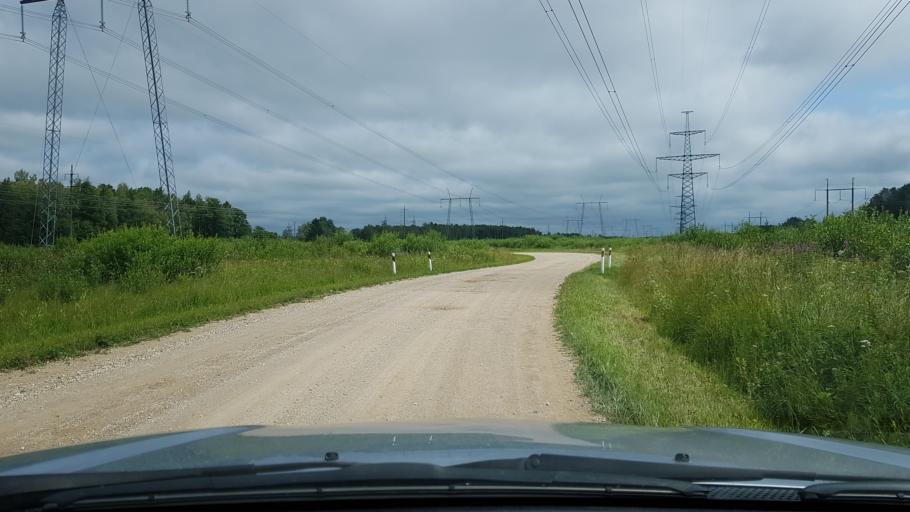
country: EE
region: Ida-Virumaa
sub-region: Narva-Joesuu linn
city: Narva-Joesuu
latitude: 59.3646
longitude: 28.0659
